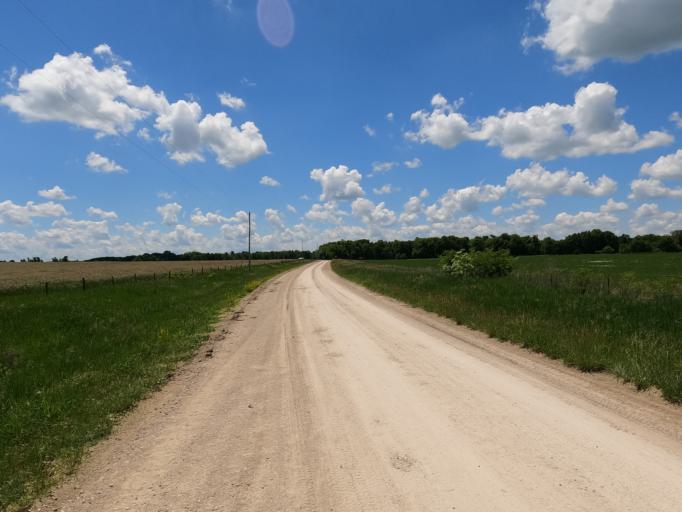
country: US
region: Kansas
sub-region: Marion County
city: Marion
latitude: 38.2334
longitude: -96.8046
